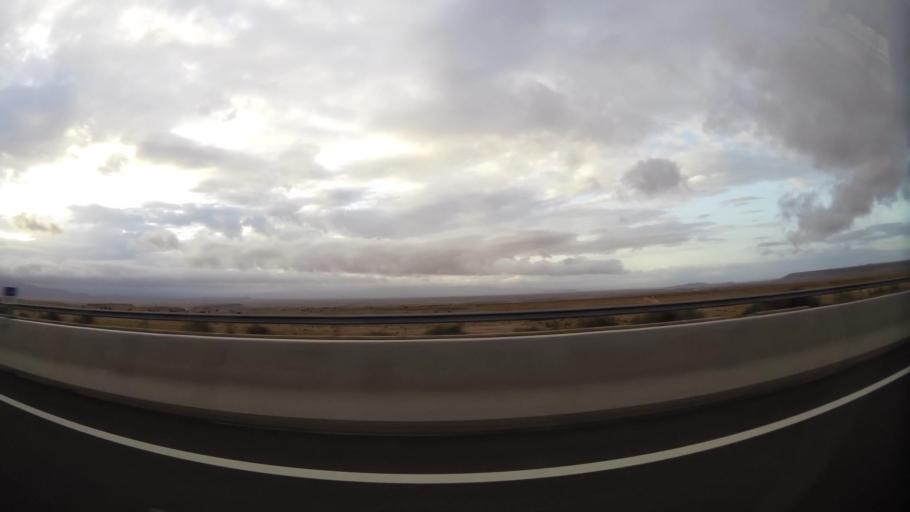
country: MA
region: Oriental
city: Taourirt
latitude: 34.4156
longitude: -3.1265
